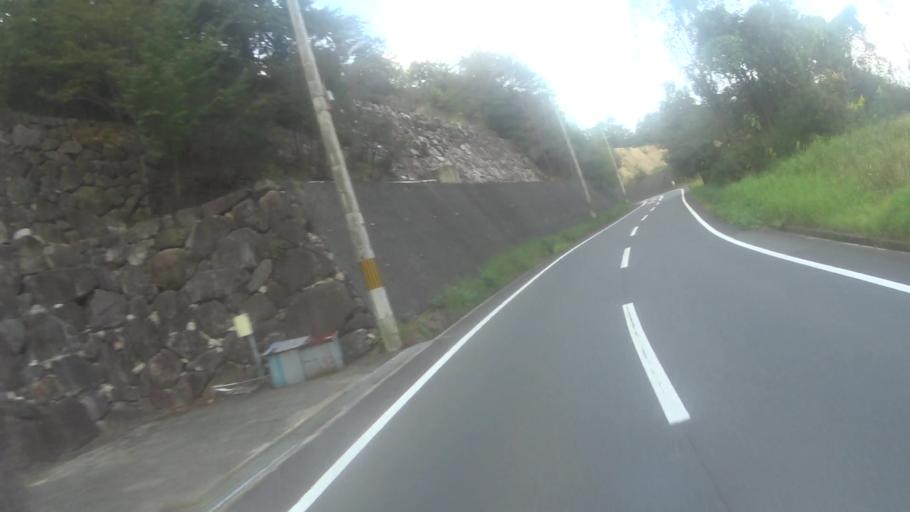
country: JP
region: Kyoto
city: Miyazu
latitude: 35.5263
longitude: 135.0920
